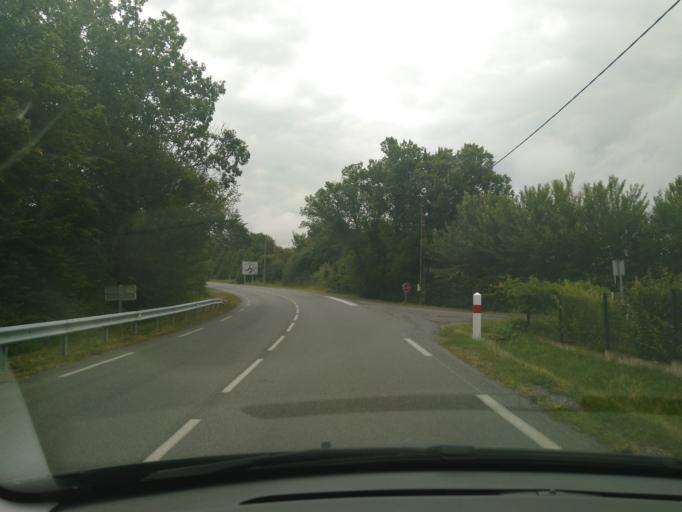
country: FR
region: Limousin
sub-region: Departement de la Correze
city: Cosnac
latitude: 45.1019
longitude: 1.5661
